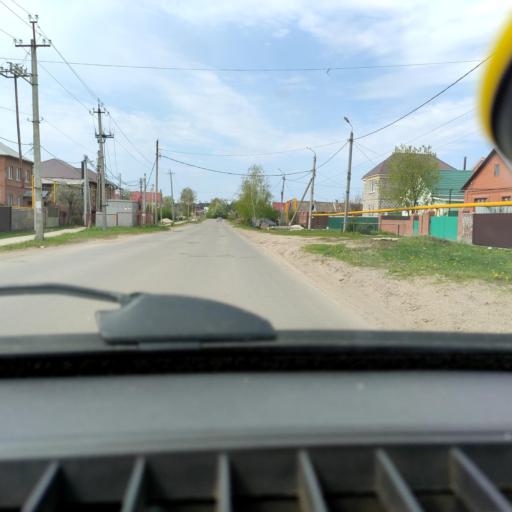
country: RU
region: Samara
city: Zhigulevsk
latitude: 53.4672
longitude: 49.6284
